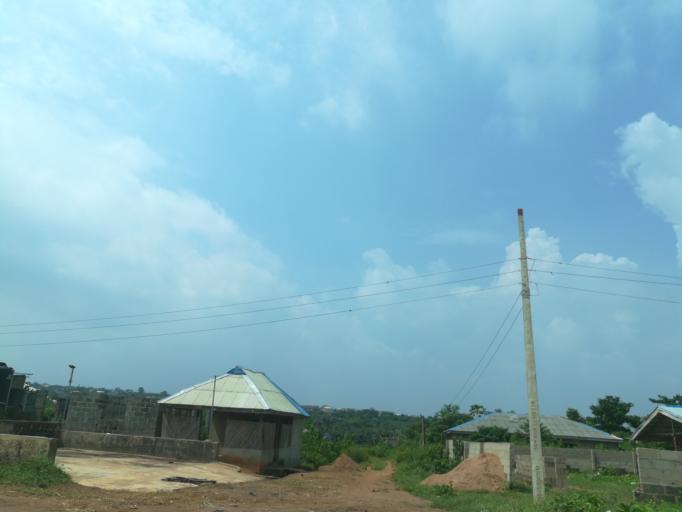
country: NG
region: Lagos
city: Ikorodu
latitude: 6.5934
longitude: 3.6392
